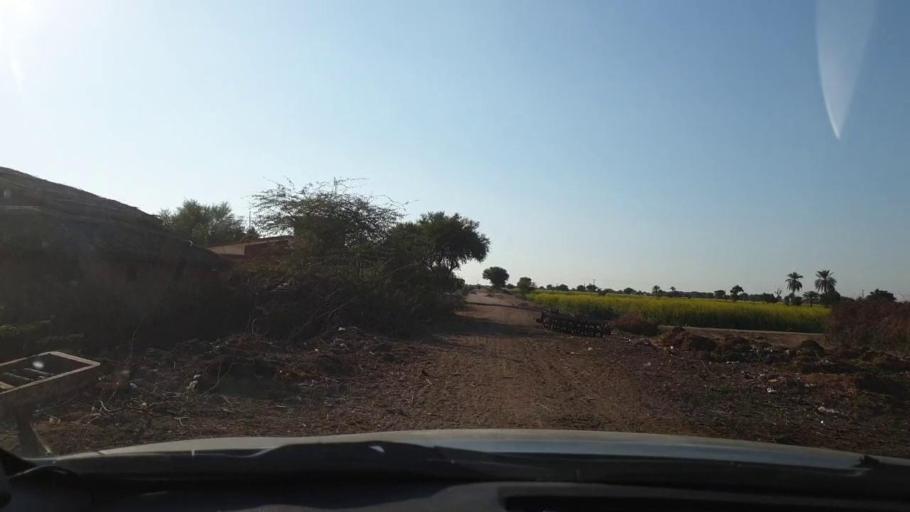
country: PK
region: Sindh
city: Jhol
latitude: 25.8690
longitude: 68.9460
